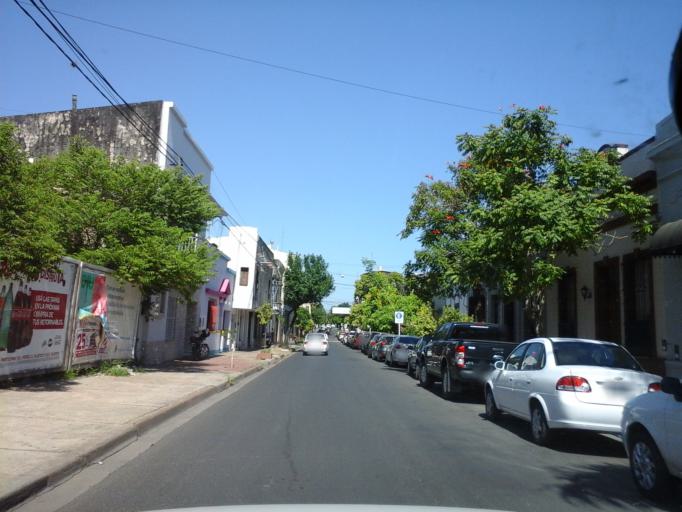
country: AR
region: Corrientes
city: Corrientes
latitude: -27.4633
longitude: -58.8327
